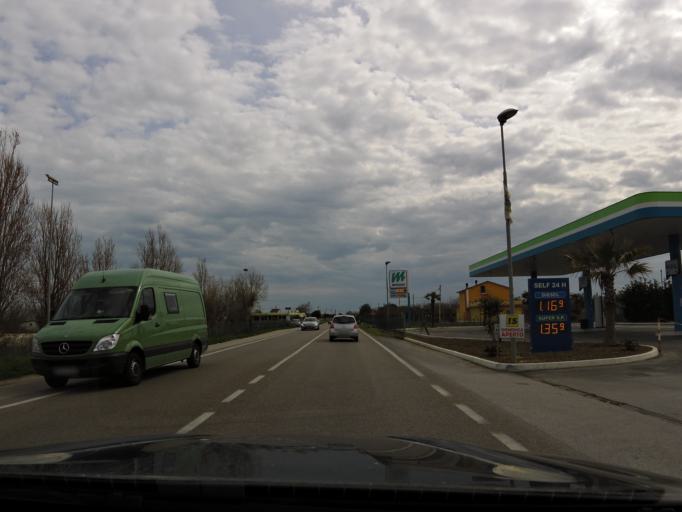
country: IT
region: The Marches
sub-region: Provincia di Macerata
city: Porto Potenza Picena
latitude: 43.3900
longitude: 13.6834
